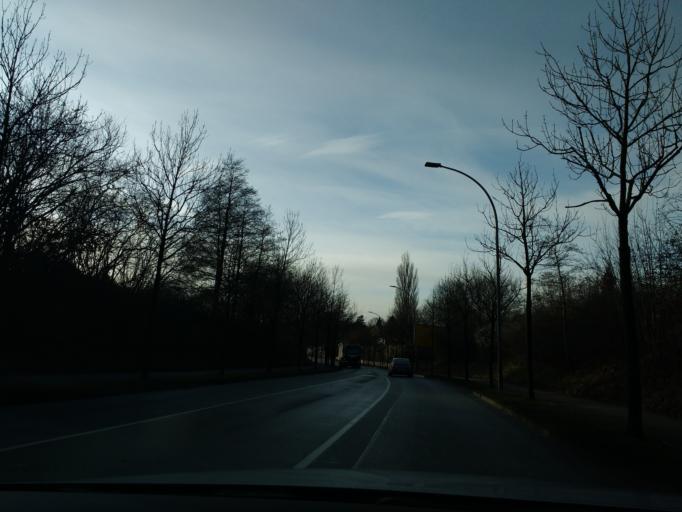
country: DE
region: Schleswig-Holstein
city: Itzehoe
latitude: 53.9306
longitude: 9.5130
